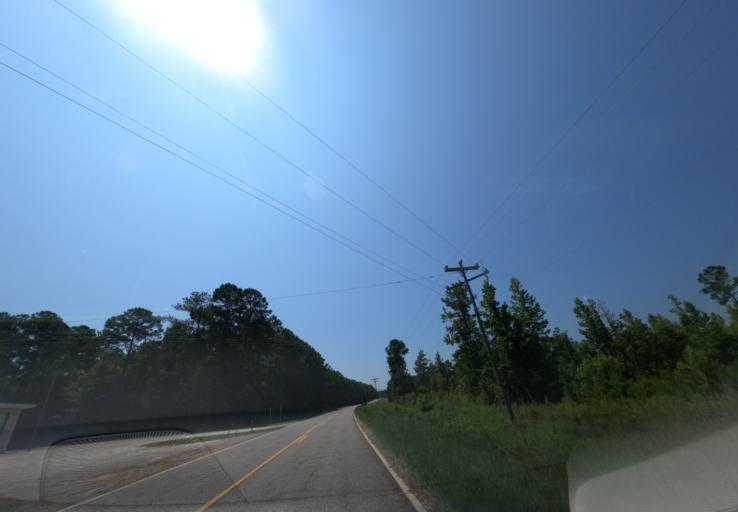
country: US
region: South Carolina
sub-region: Greenwood County
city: Greenwood
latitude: 34.0419
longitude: -82.1310
